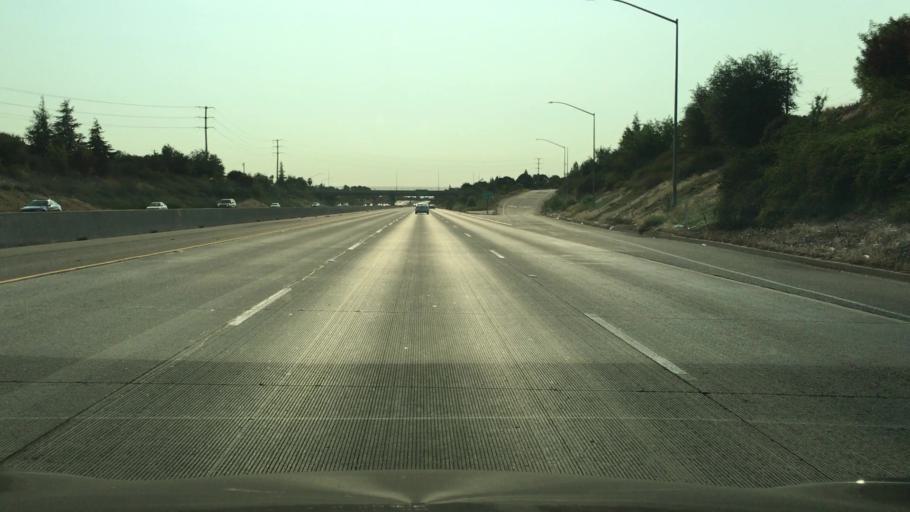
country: US
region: California
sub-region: Fresno County
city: Sunnyside
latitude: 36.7533
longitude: -119.7131
